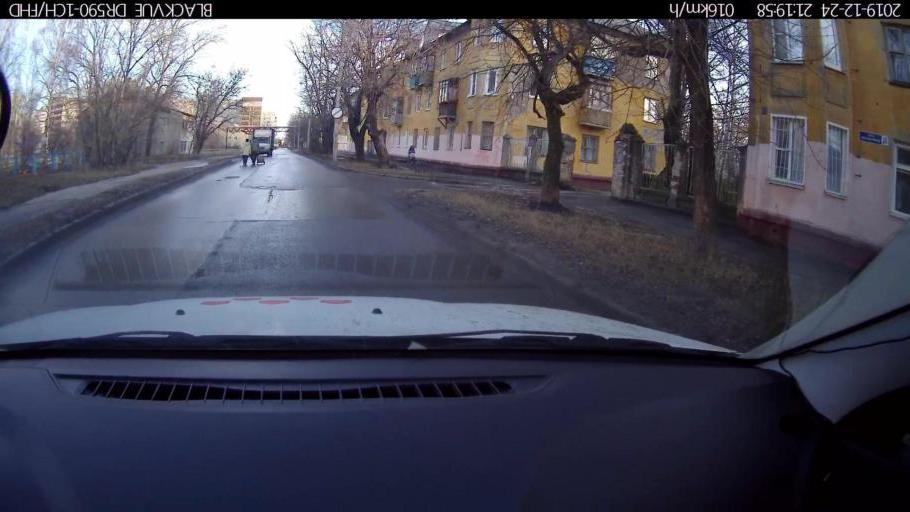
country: RU
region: Nizjnij Novgorod
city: Nizhniy Novgorod
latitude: 56.2676
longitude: 43.8838
